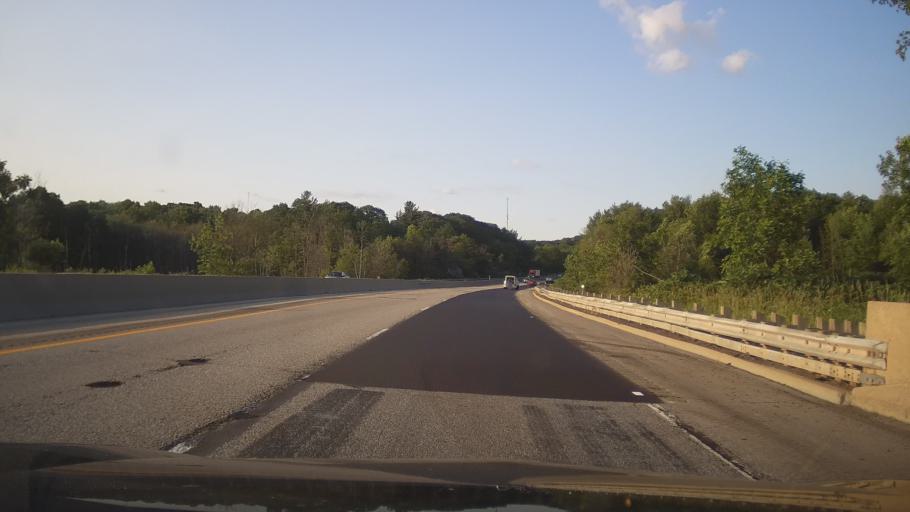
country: CA
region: Ontario
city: Brockville
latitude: 44.5799
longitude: -75.7334
